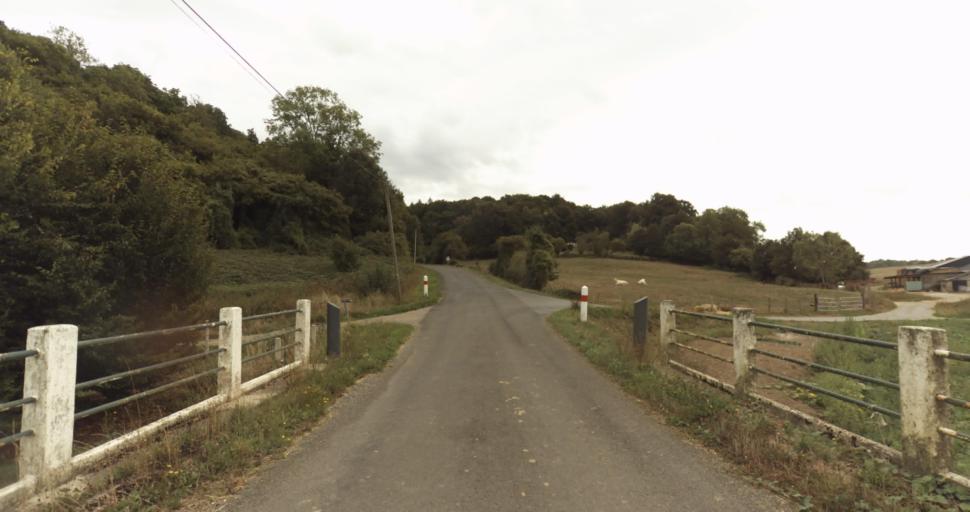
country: FR
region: Lower Normandy
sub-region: Departement de l'Orne
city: Vimoutiers
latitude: 48.9324
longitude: 0.3219
